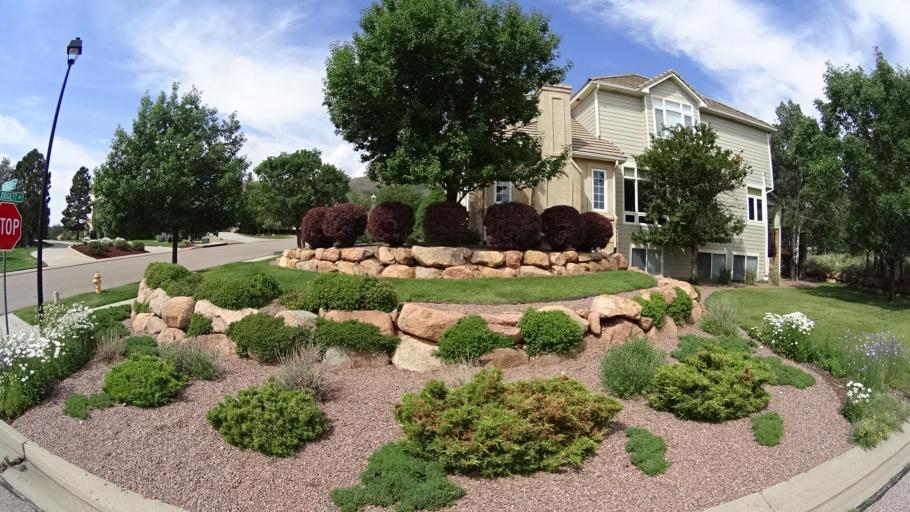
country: US
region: Colorado
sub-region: El Paso County
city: Air Force Academy
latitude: 38.9533
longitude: -104.8820
